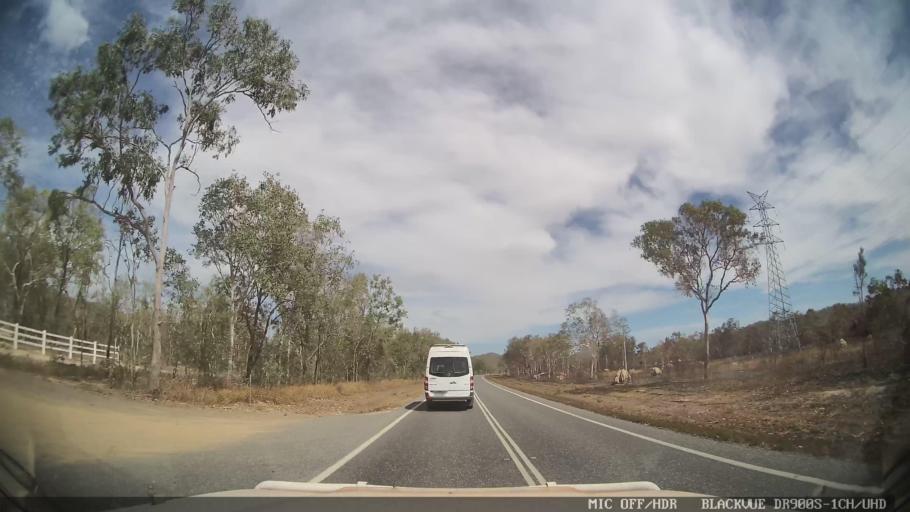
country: AU
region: Queensland
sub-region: Cairns
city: Port Douglas
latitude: -16.7191
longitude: 145.3528
